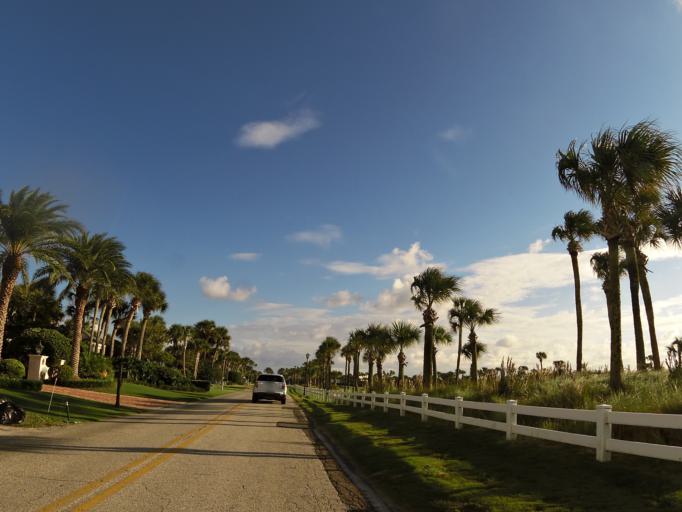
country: US
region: Florida
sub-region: Saint Johns County
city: Ponte Vedra Beach
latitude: 30.2470
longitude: -81.3801
